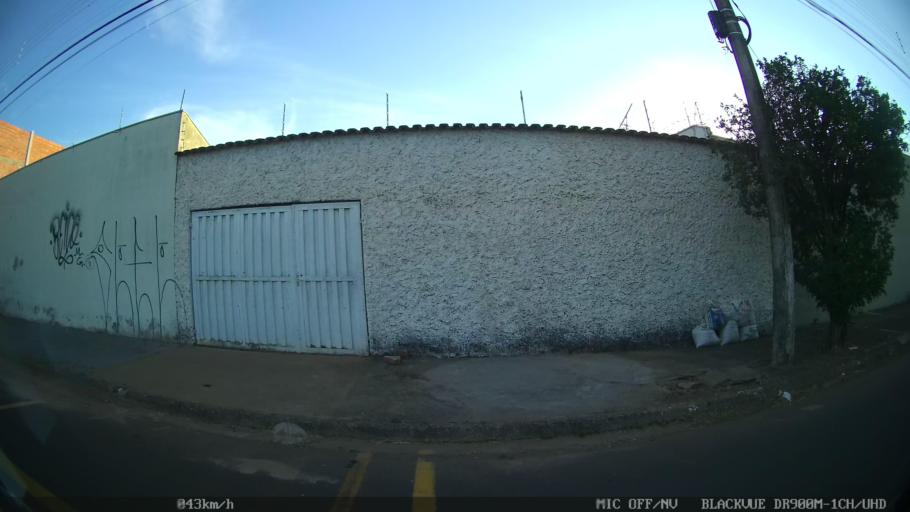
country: BR
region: Sao Paulo
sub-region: Franca
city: Franca
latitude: -20.5167
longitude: -47.3955
